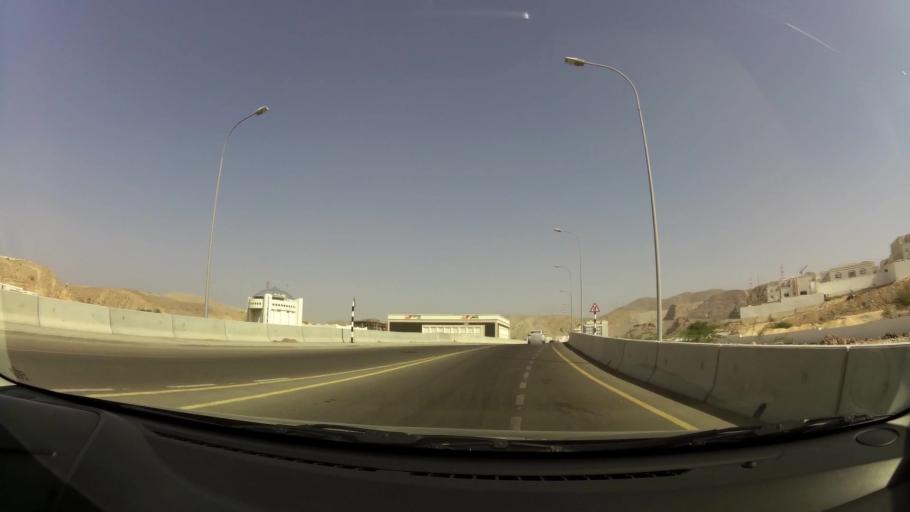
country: OM
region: Muhafazat Masqat
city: Muscat
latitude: 23.6083
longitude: 58.4971
